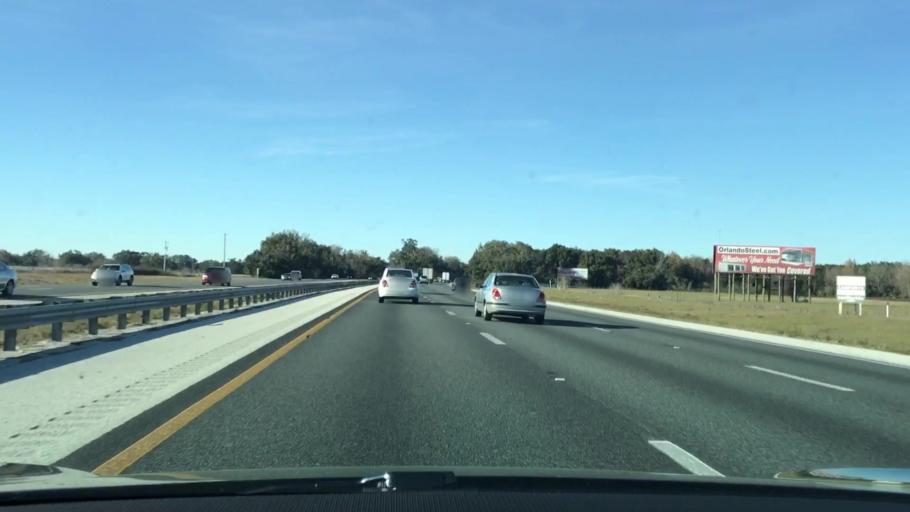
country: US
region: Florida
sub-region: Sumter County
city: Wildwood
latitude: 28.9082
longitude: -82.1078
